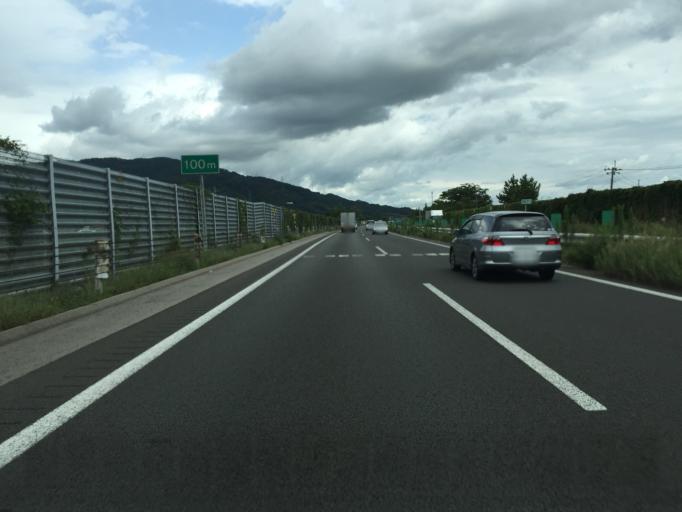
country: JP
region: Fukushima
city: Fukushima-shi
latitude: 37.8199
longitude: 140.4746
